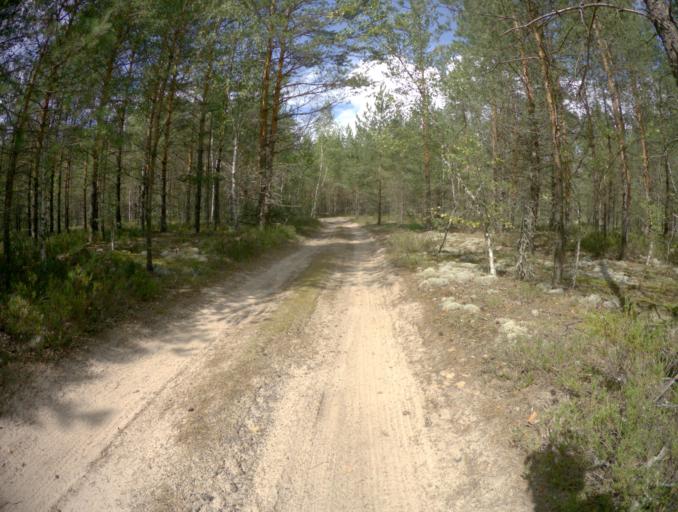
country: RU
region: Vladimir
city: Raduzhnyy
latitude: 55.9587
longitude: 40.2022
